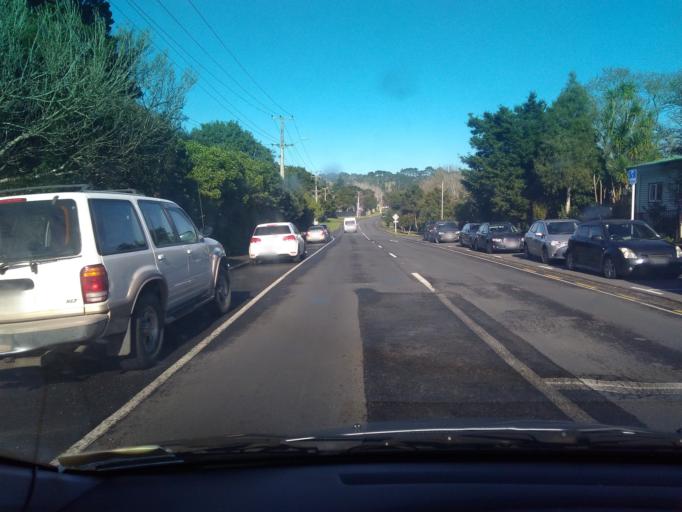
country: NZ
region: Auckland
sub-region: Auckland
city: Muriwai Beach
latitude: -36.7705
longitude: 174.4916
